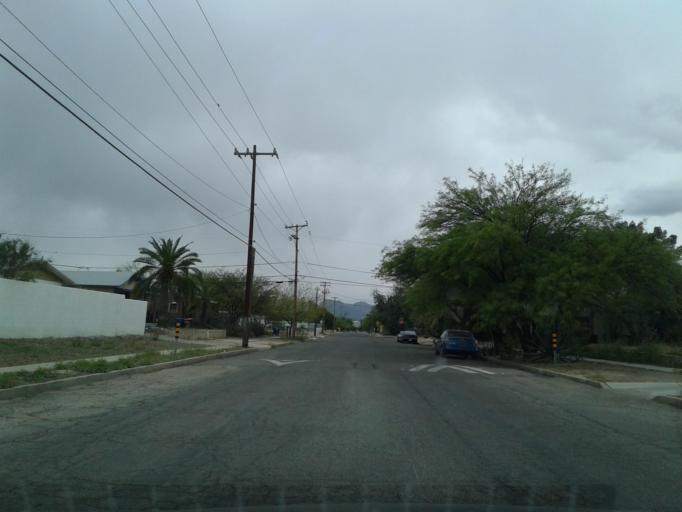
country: US
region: Arizona
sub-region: Pima County
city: South Tucson
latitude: 32.2372
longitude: -110.9673
